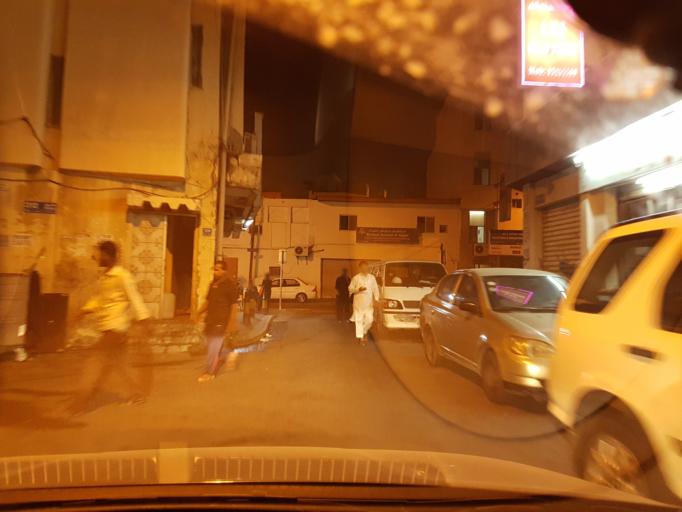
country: BH
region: Manama
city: Manama
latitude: 26.2276
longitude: 50.5708
